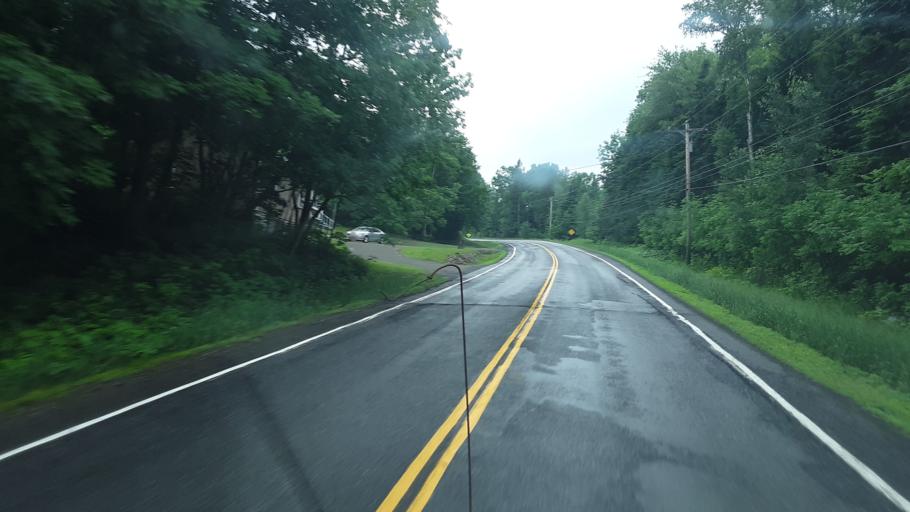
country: US
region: Maine
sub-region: Penobscot County
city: Patten
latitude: 46.0705
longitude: -68.4375
